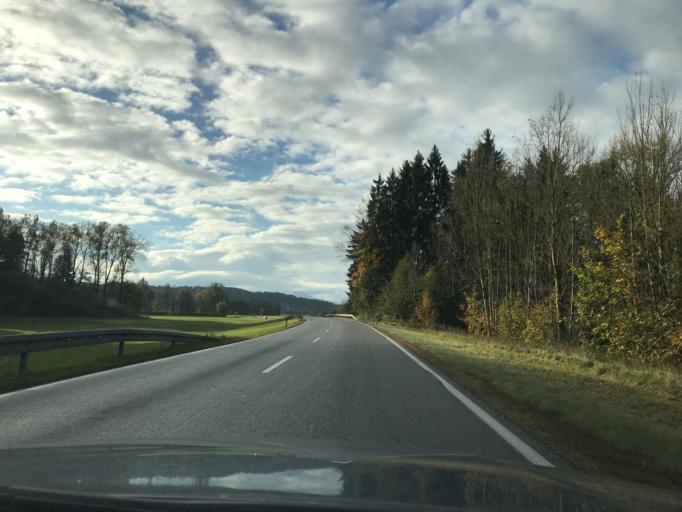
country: DE
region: Bavaria
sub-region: Upper Bavaria
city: Geretsried
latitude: 47.8421
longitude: 11.5268
